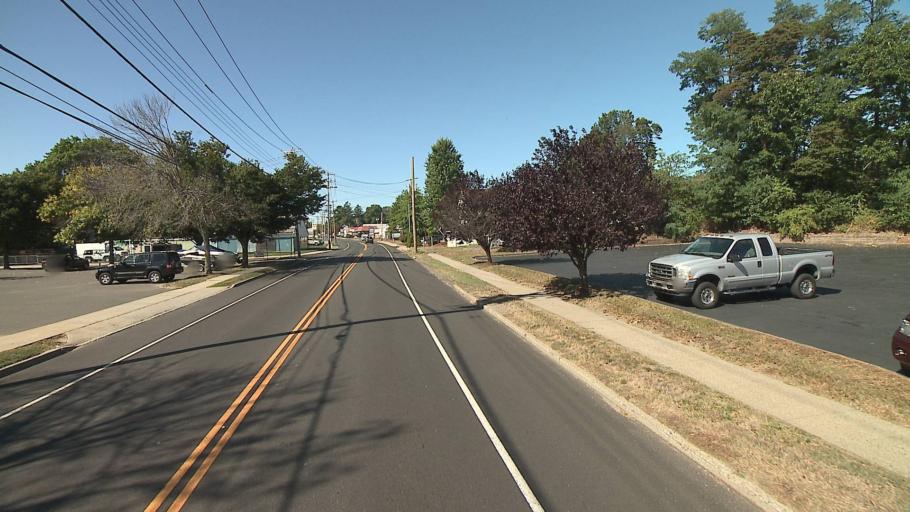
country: US
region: Connecticut
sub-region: New Haven County
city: Milford
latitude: 41.2238
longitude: -73.0385
